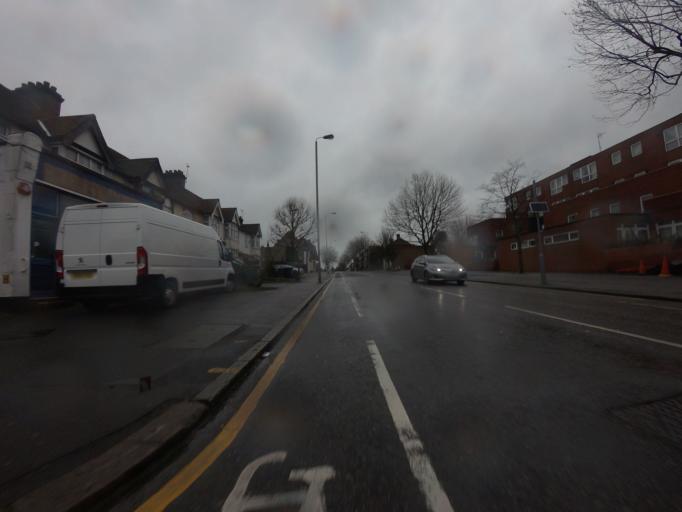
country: GB
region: England
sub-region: Greater London
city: Walthamstow
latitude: 51.6146
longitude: -0.0175
